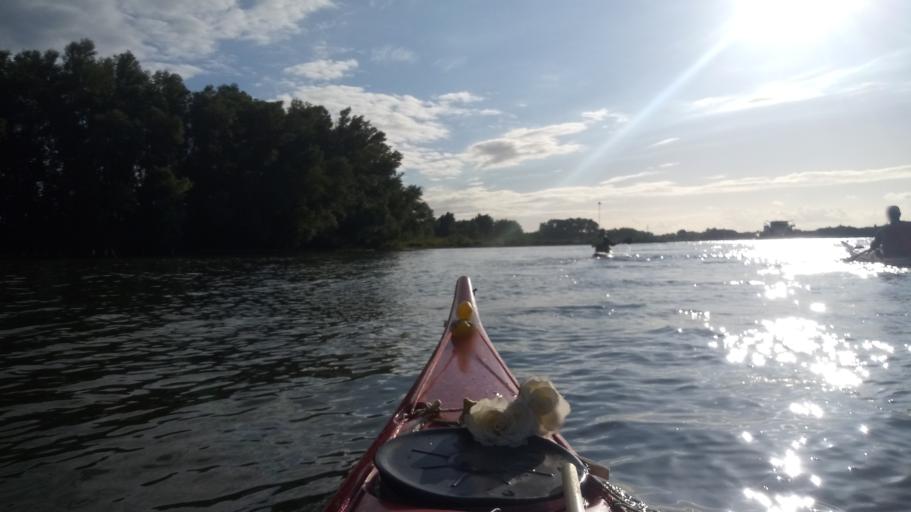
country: NL
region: Gelderland
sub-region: Gemeente Zaltbommel
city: Zaltbommel
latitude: 51.8104
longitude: 5.2246
